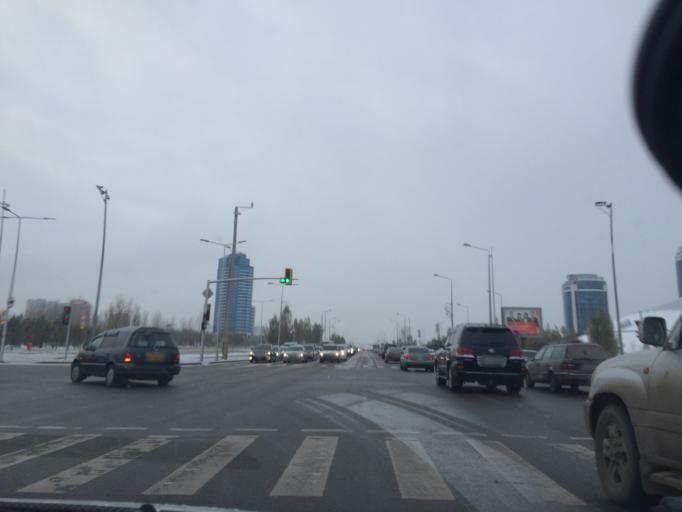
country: KZ
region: Astana Qalasy
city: Astana
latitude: 51.1346
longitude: 71.4076
